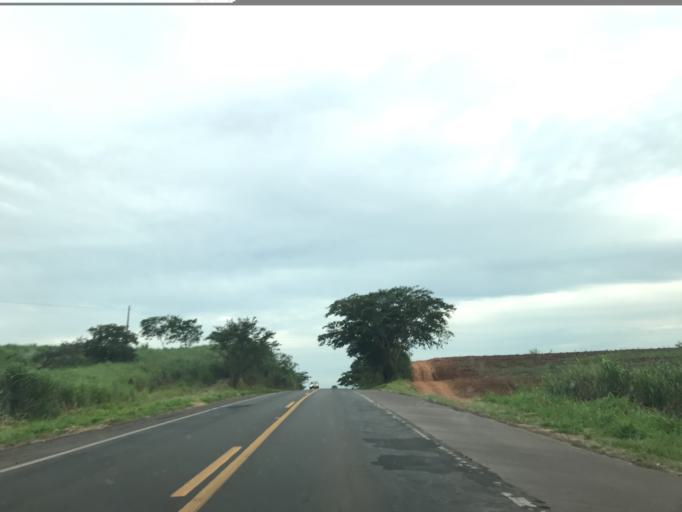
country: BR
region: Sao Paulo
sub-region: Birigui
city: Birigui
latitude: -21.5942
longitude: -50.4632
